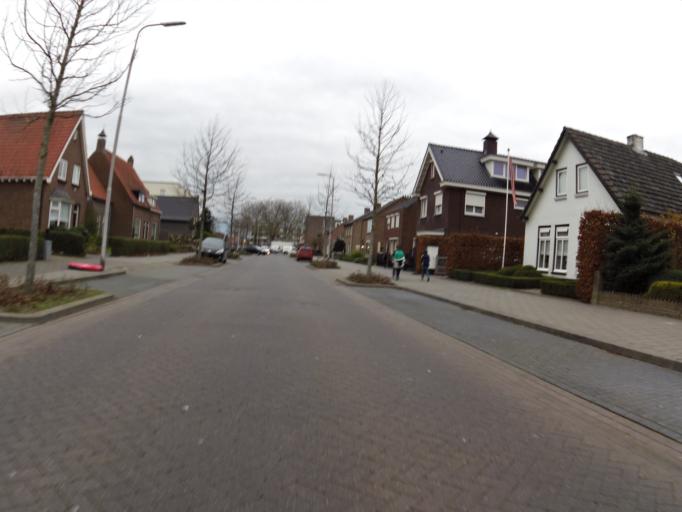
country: NL
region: North Brabant
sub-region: Gemeente Oss
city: Oss
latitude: 51.7568
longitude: 5.5393
